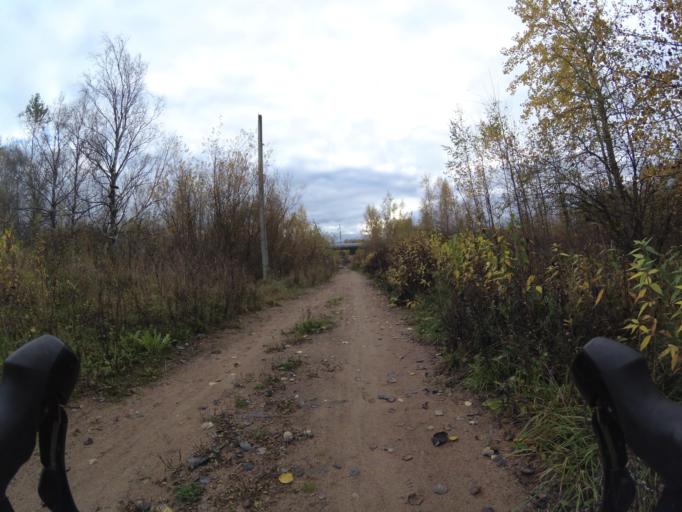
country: RU
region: St.-Petersburg
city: Lakhtinskiy
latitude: 60.0057
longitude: 30.1441
